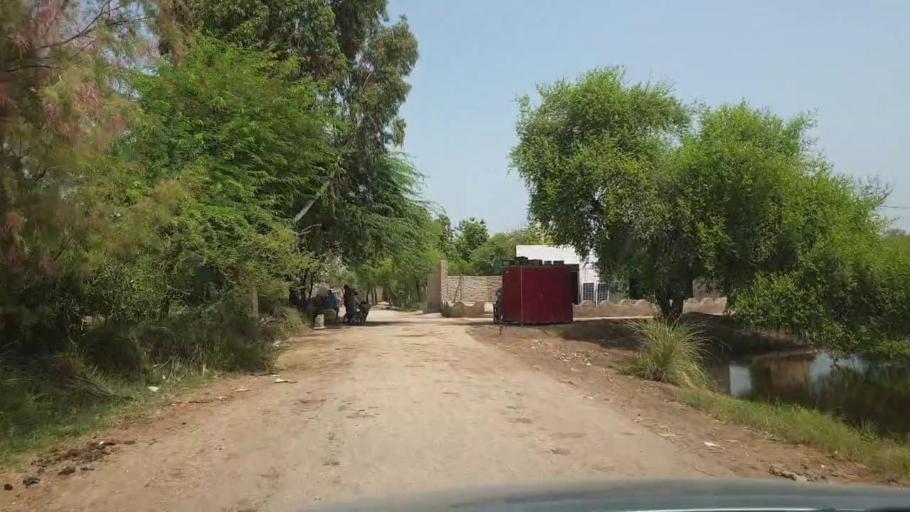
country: PK
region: Sindh
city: Madeji
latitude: 27.8083
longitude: 68.5200
